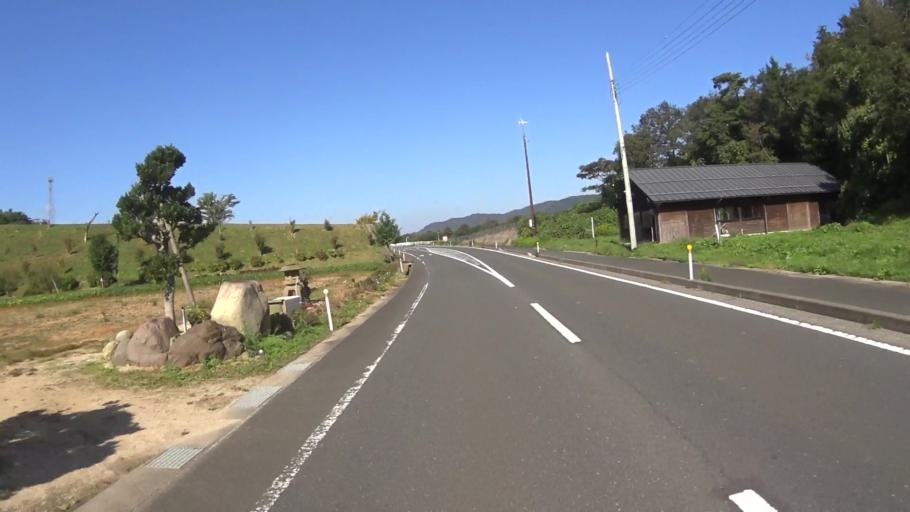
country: JP
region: Kyoto
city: Miyazu
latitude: 35.6669
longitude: 135.1009
